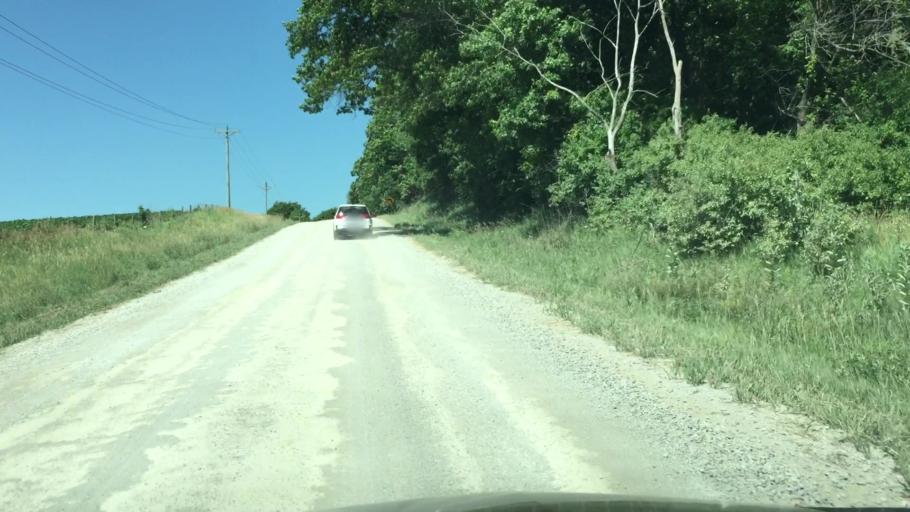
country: US
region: Iowa
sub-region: Linn County
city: Ely
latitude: 41.8329
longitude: -91.5859
